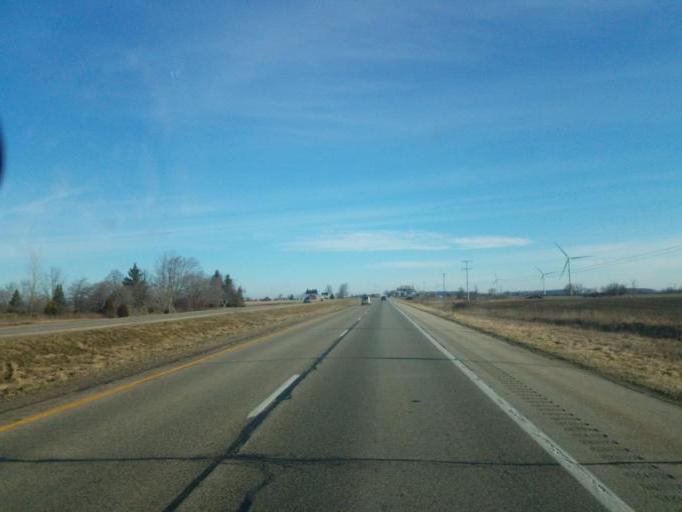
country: US
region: Michigan
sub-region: Gratiot County
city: Ithaca
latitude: 43.2605
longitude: -84.5631
